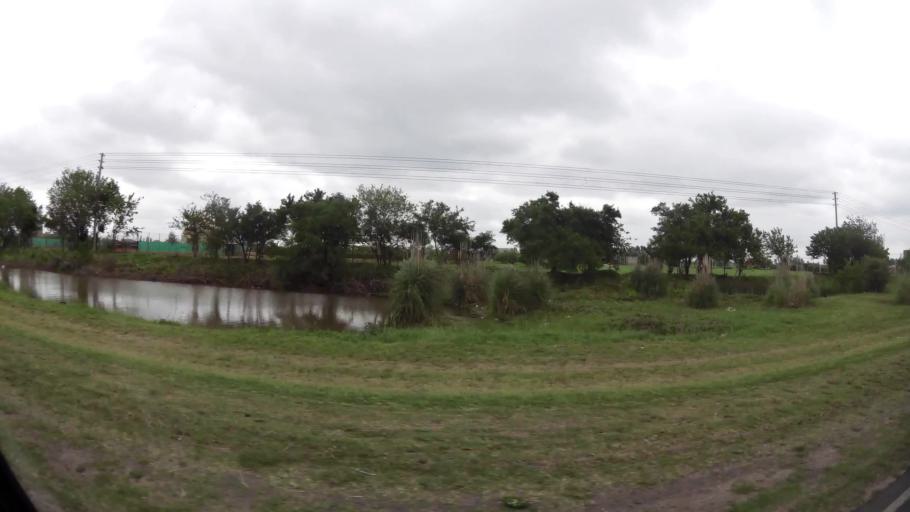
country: AR
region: Buenos Aires
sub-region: Partido de San Vicente
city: San Vicente
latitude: -34.9586
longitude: -58.4647
